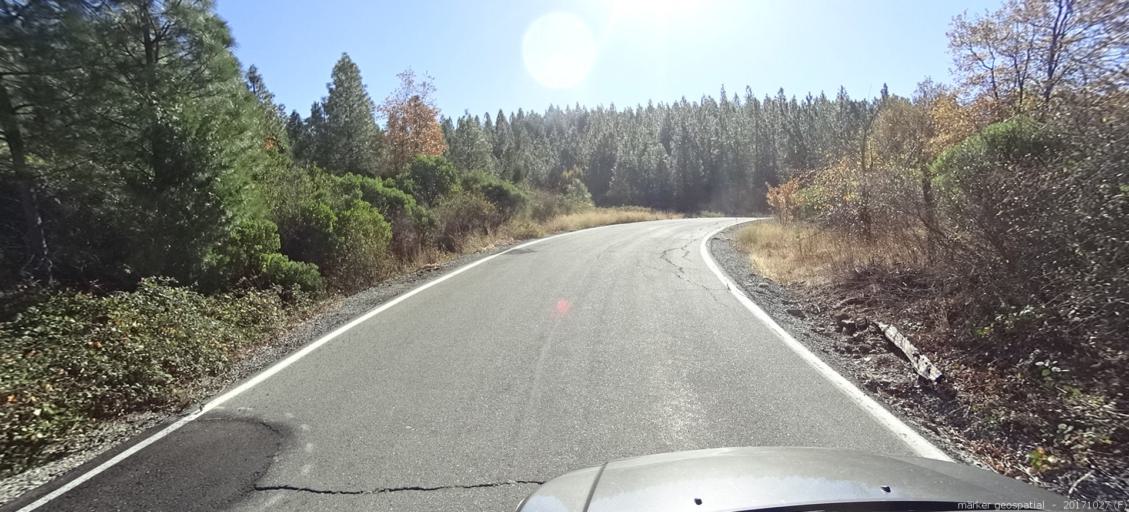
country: US
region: California
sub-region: Shasta County
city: Burney
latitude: 40.7878
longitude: -121.9098
